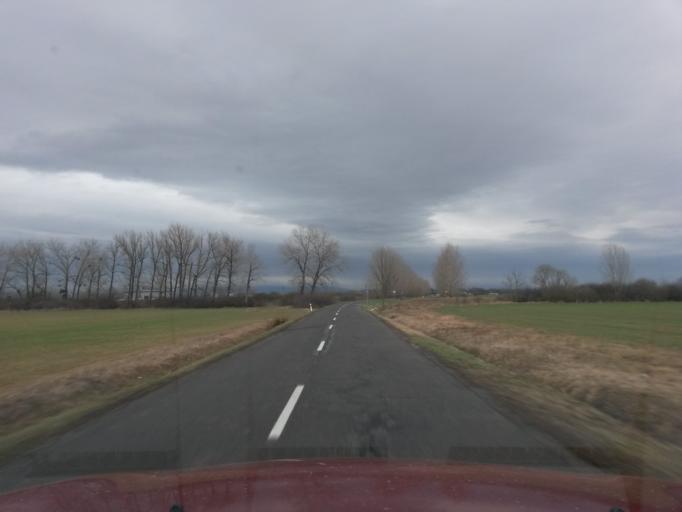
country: SK
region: Kosicky
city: Michalovce
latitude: 48.6637
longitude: 22.0054
